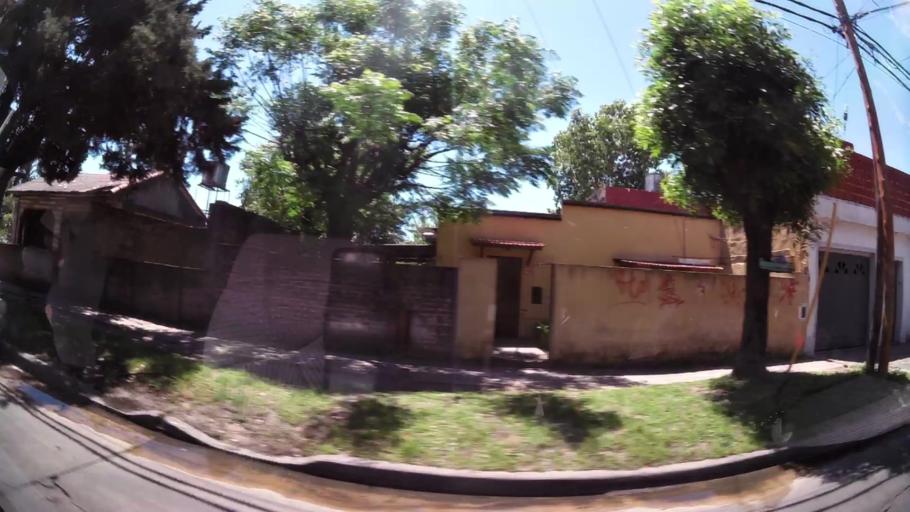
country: AR
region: Buenos Aires
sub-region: Partido de Tigre
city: Tigre
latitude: -34.4940
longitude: -58.6378
